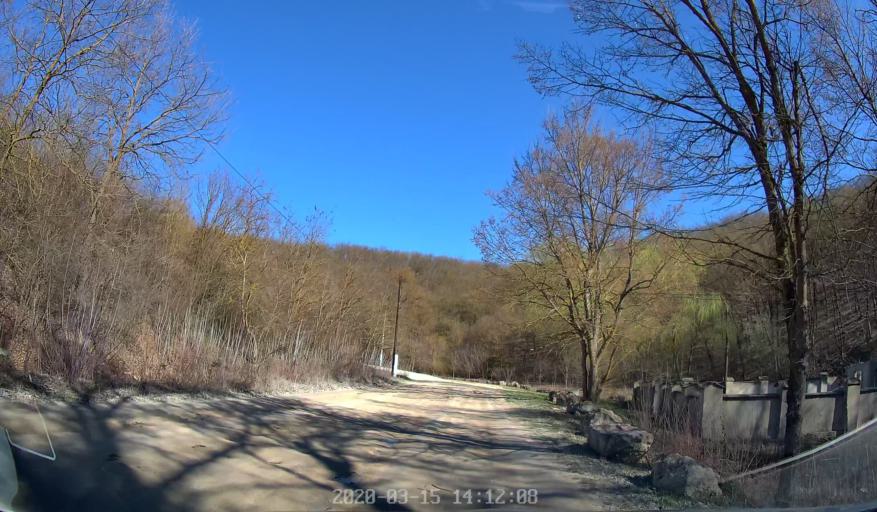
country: MD
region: Orhei
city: Orhei
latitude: 47.3139
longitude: 28.9369
